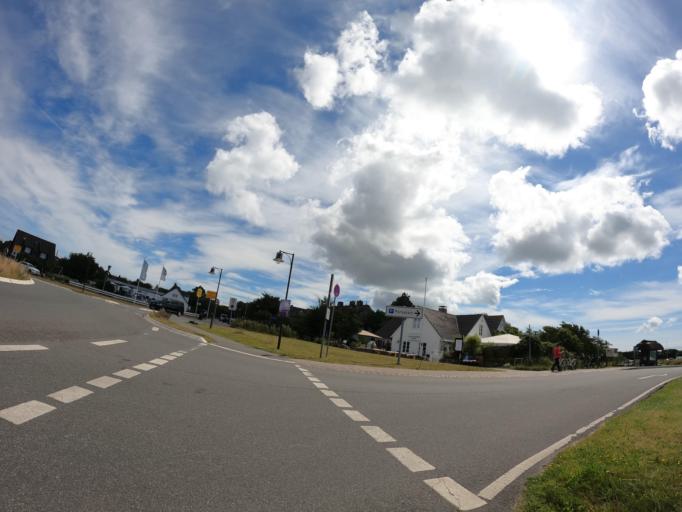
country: DE
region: Schleswig-Holstein
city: Keitum
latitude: 54.8964
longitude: 8.3635
